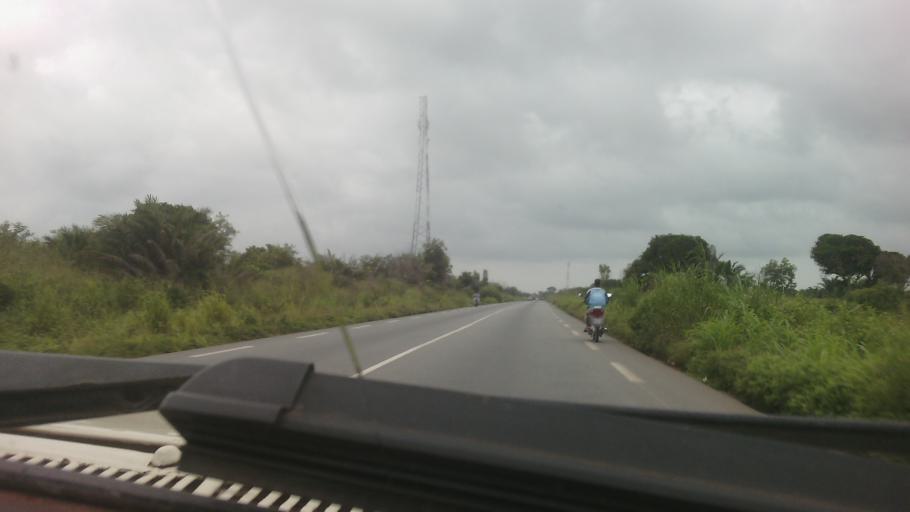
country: BJ
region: Atlantique
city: Ouidah
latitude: 6.3938
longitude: 1.9872
